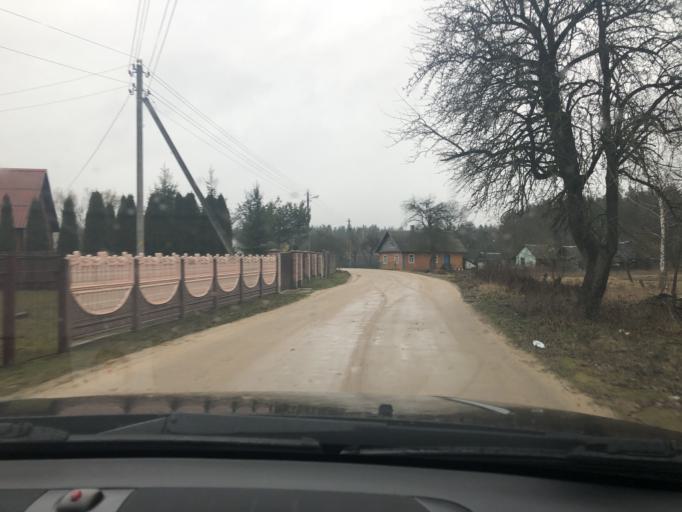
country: BY
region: Grodnenskaya
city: Skidal'
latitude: 53.8574
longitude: 24.2513
